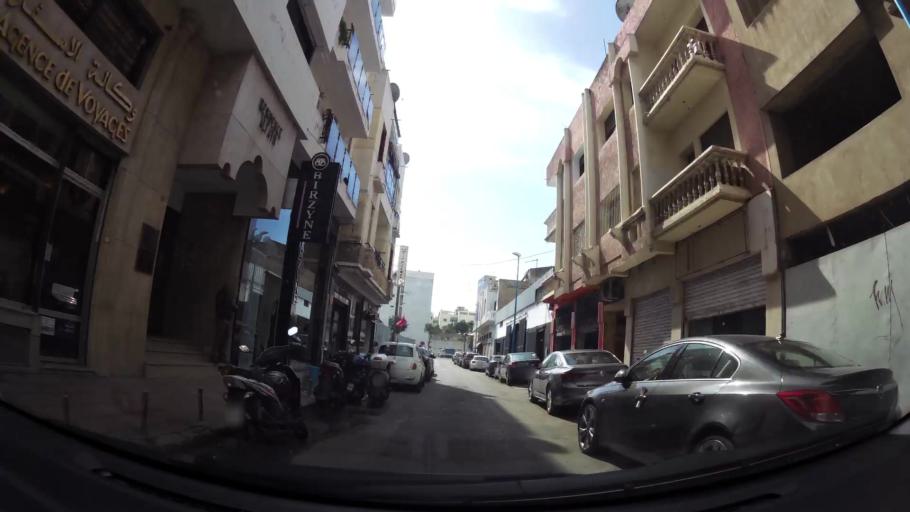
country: MA
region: Grand Casablanca
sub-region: Casablanca
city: Casablanca
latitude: 33.5840
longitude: -7.6327
